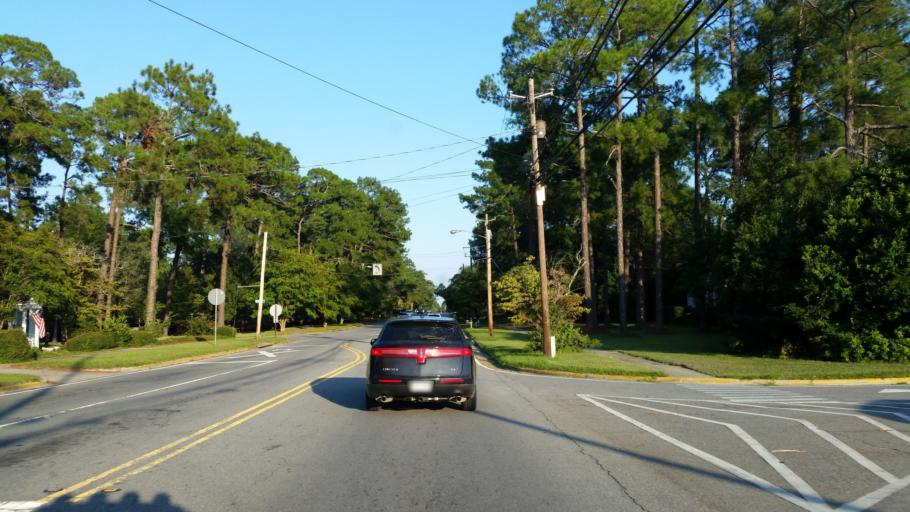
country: US
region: Georgia
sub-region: Tift County
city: Tifton
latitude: 31.4626
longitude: -83.5169
